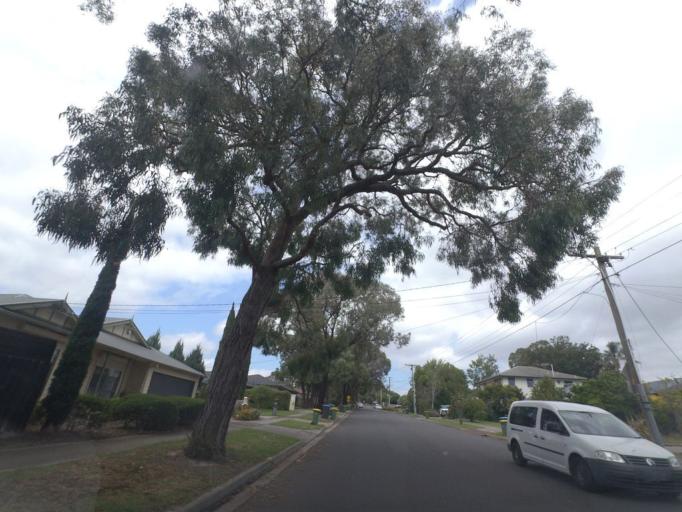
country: AU
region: Victoria
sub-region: Knox
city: Boronia
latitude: -37.8730
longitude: 145.2794
